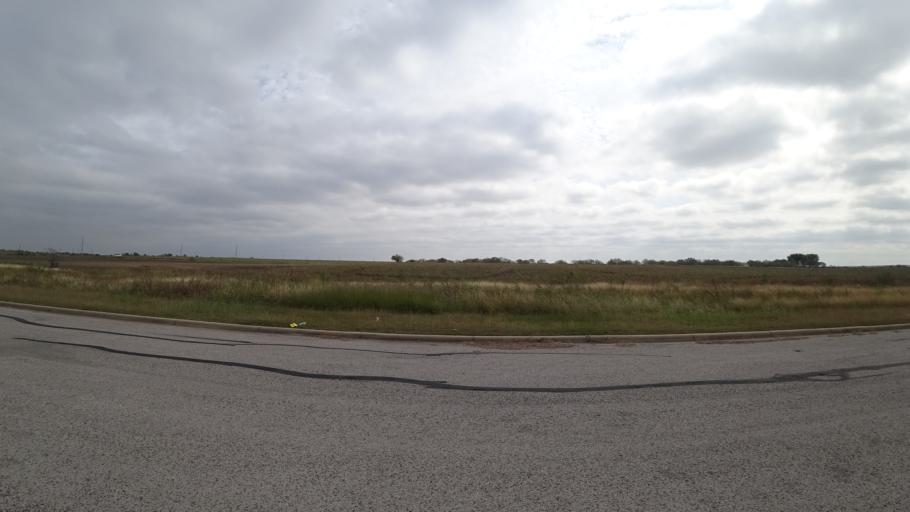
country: US
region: Texas
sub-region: Travis County
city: Manor
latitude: 30.3724
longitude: -97.6074
